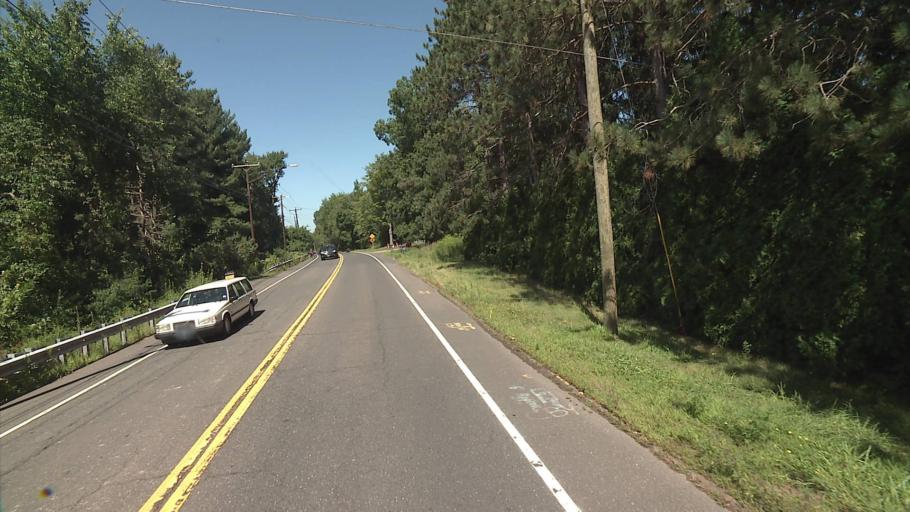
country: US
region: Connecticut
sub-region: Hartford County
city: Windsor Locks
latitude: 41.9544
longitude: -72.6275
